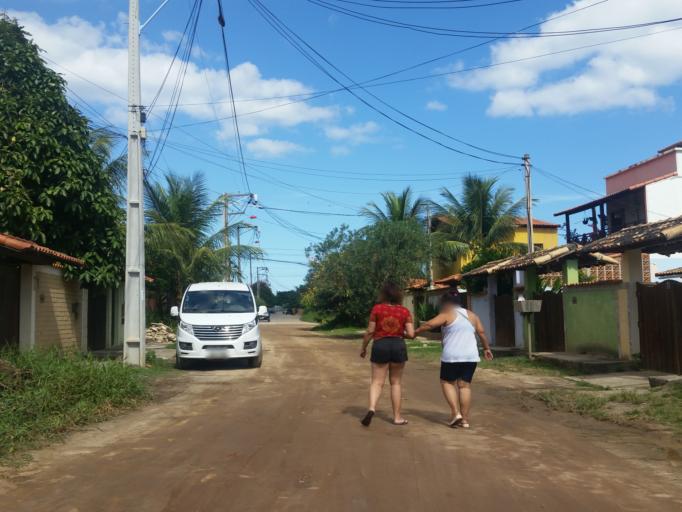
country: BR
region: Rio de Janeiro
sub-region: Marica
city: Marica
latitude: -22.9590
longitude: -42.9667
